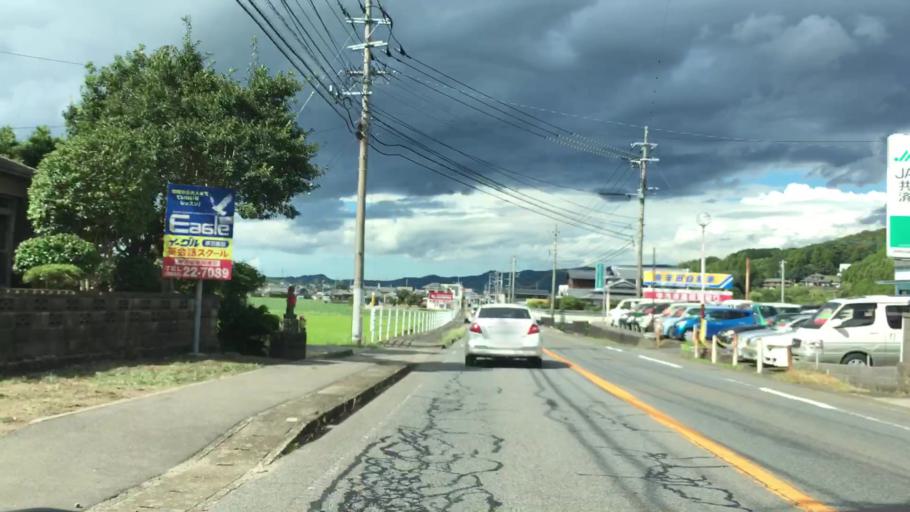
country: JP
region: Saga Prefecture
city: Imaricho-ko
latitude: 33.2463
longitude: 129.8516
